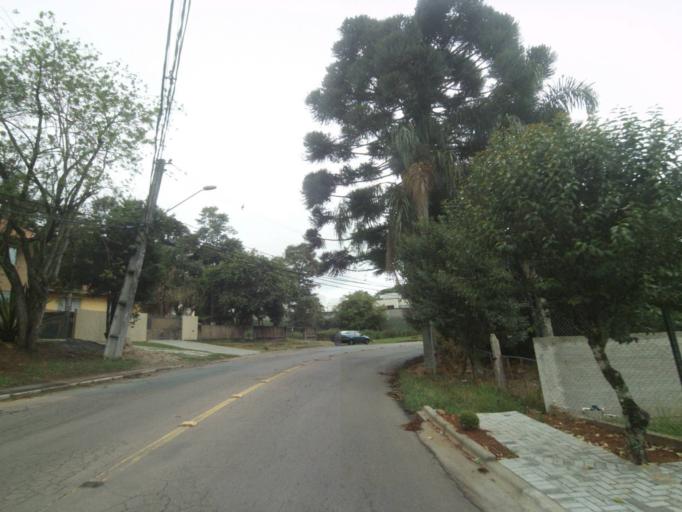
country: BR
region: Parana
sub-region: Curitiba
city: Curitiba
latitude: -25.4490
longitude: -49.3343
